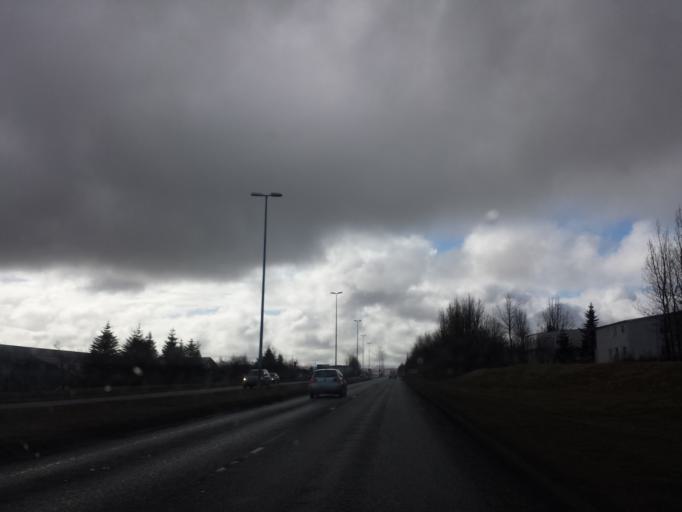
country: IS
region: Capital Region
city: Reykjavik
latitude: 64.1365
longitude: -21.8503
